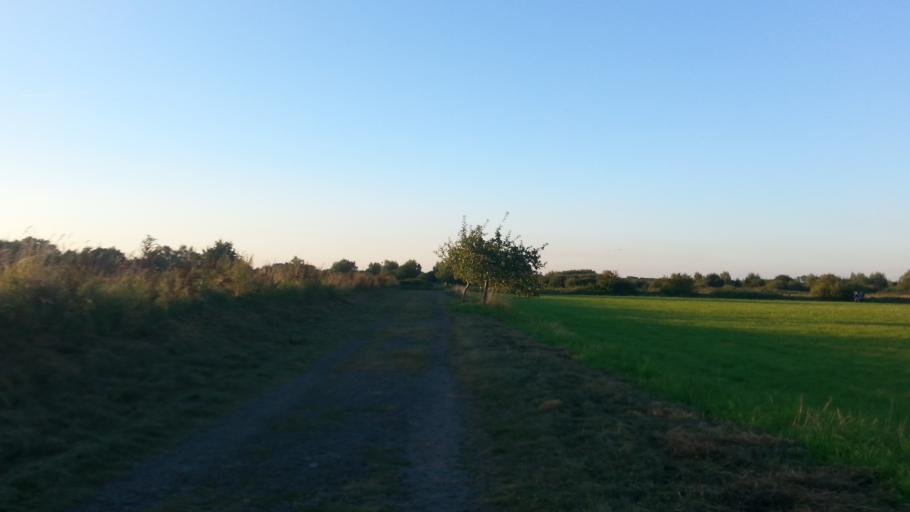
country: DE
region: North Rhine-Westphalia
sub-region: Regierungsbezirk Munster
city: Muenster
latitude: 52.0162
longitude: 7.6484
